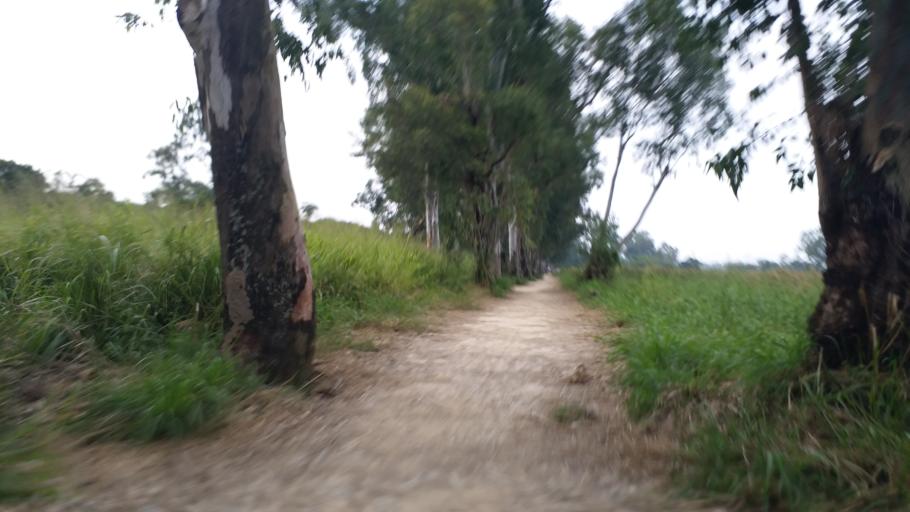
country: HK
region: Yuen Long
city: Yuen Long Kau Hui
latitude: 22.4558
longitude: 114.0347
